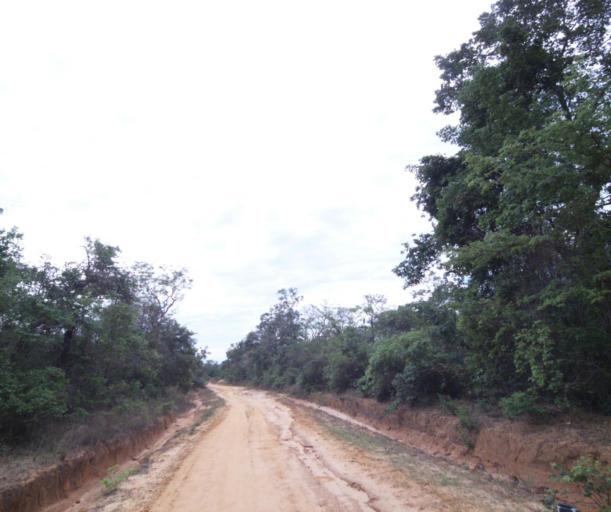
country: BR
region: Bahia
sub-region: Carinhanha
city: Carinhanha
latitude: -14.2483
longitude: -44.3750
